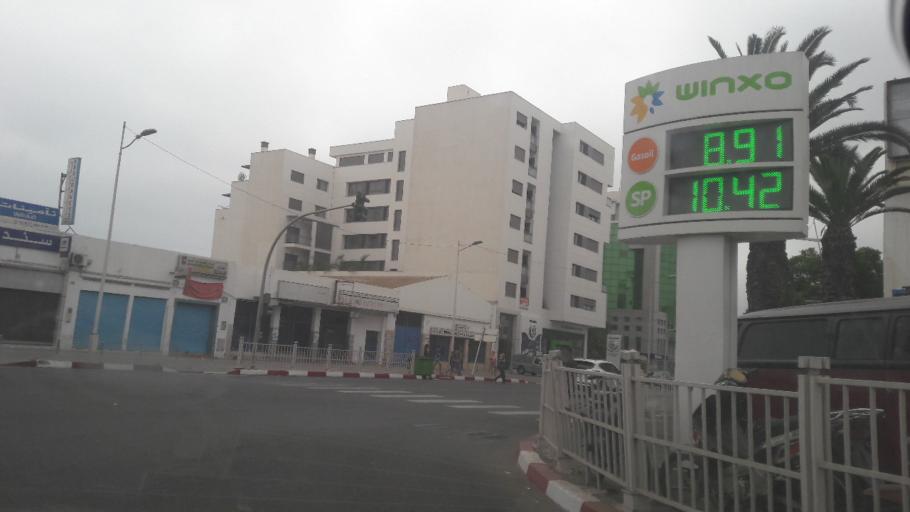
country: MA
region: Souss-Massa-Draa
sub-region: Agadir-Ida-ou-Tnan
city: Agadir
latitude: 30.4120
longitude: -9.5910
